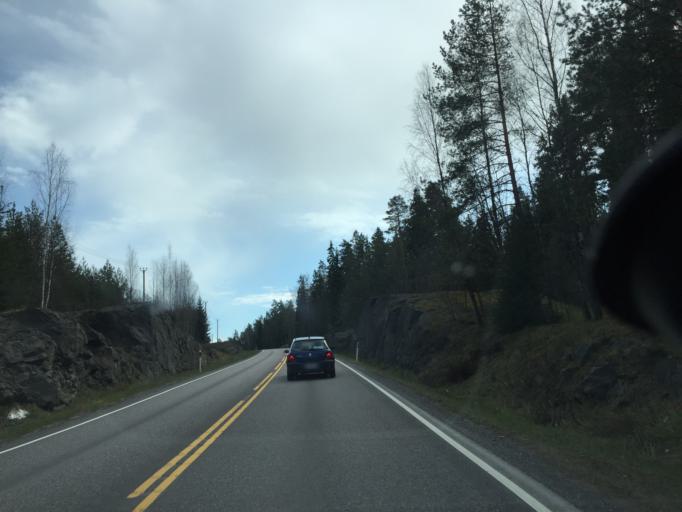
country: FI
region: Uusimaa
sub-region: Raaseporin
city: Ekenaes
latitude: 60.0310
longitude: 23.3686
